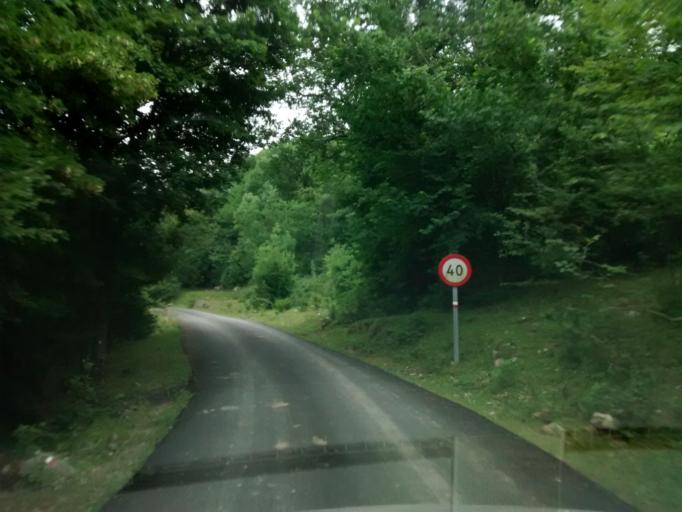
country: ES
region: Aragon
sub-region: Provincia de Huesca
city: Puertolas
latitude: 42.5940
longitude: 0.1263
